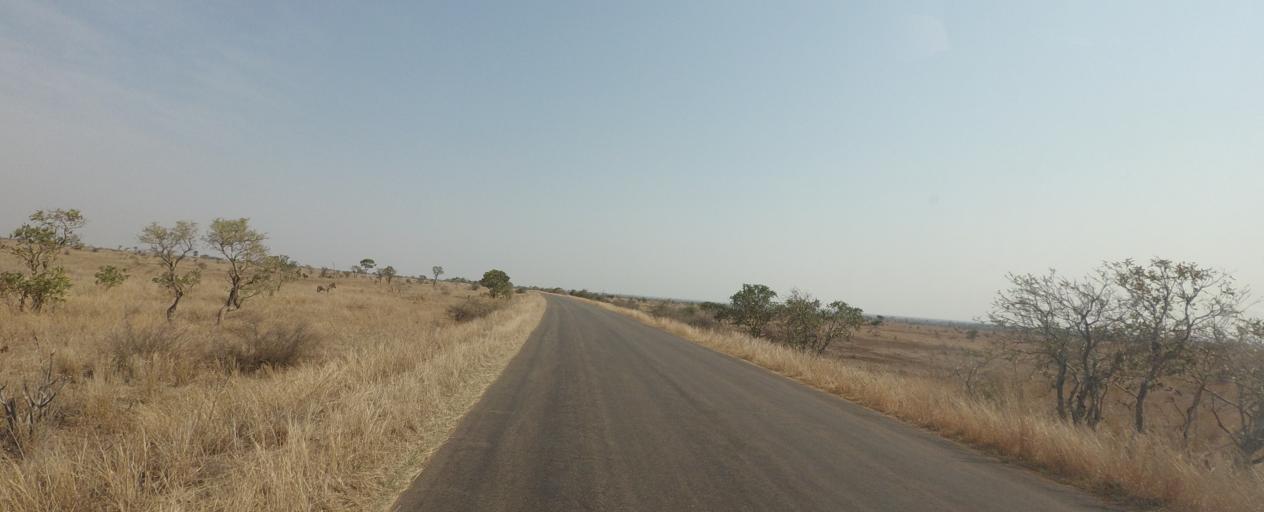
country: ZA
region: Limpopo
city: Thulamahashi
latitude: -24.3282
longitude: 31.7552
